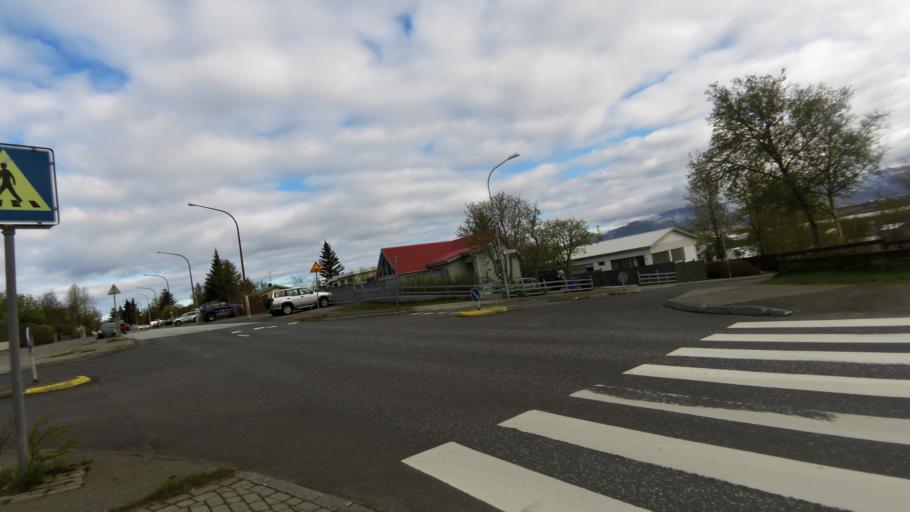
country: IS
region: Capital Region
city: Reykjavik
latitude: 64.1232
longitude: -21.8560
